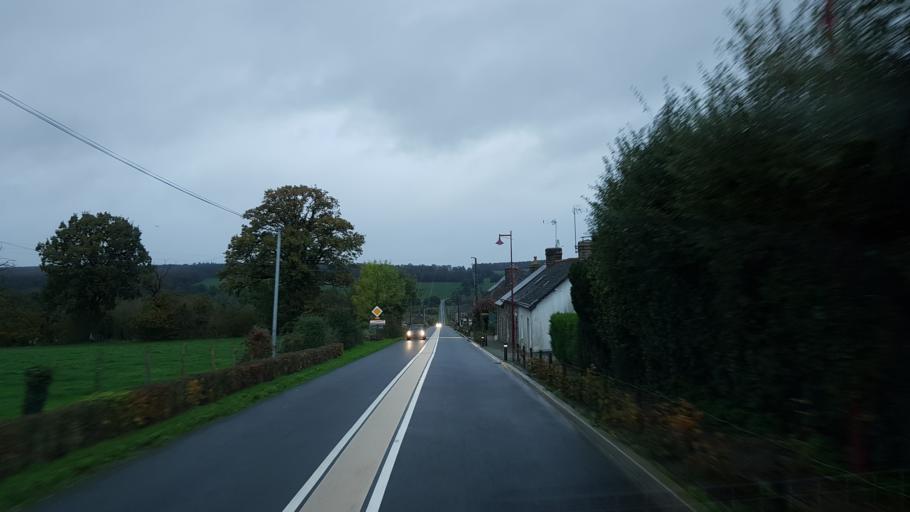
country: FR
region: Pays de la Loire
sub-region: Departement de la Mayenne
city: Juvigne
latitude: 48.2059
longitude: -1.0543
